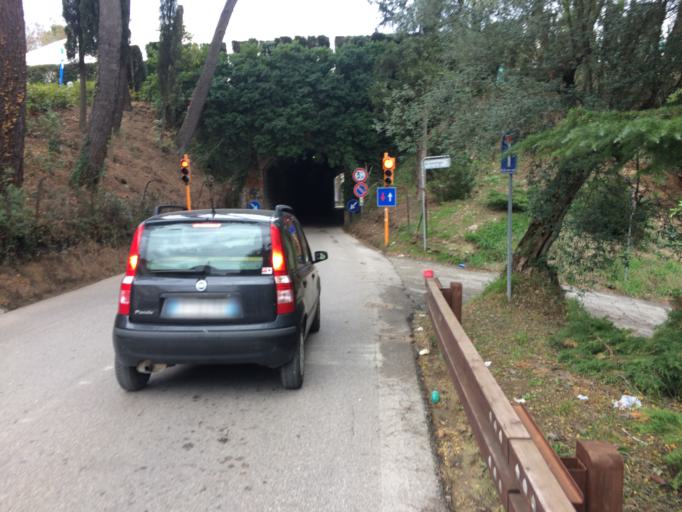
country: IT
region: Umbria
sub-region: Provincia di Perugia
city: Perugia
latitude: 43.1029
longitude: 12.3963
